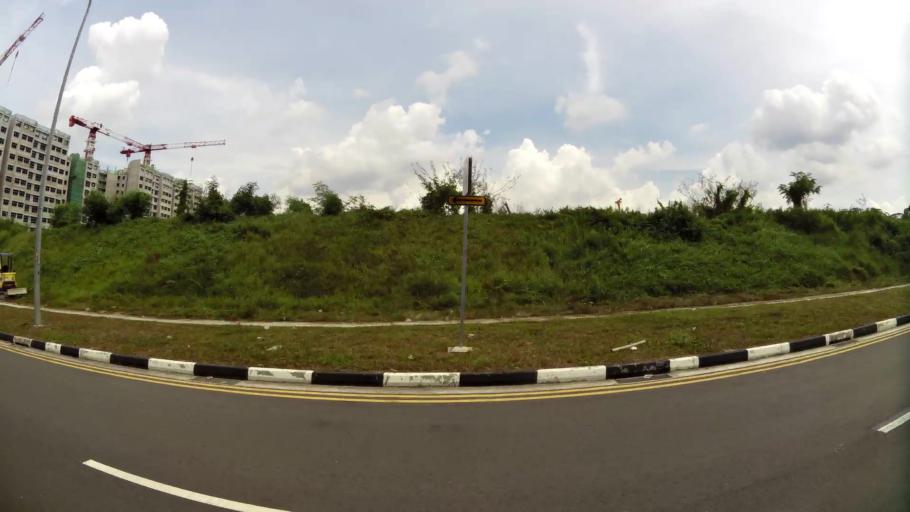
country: MY
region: Johor
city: Johor Bahru
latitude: 1.3556
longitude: 103.7406
